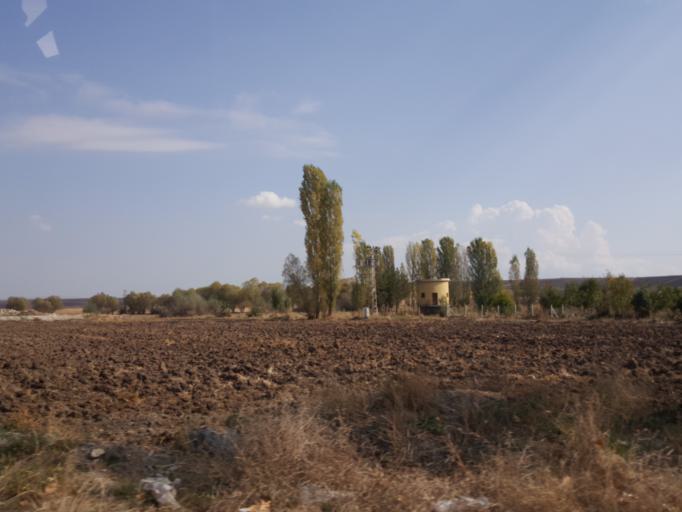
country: TR
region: Corum
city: Alaca
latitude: 40.1522
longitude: 34.8537
